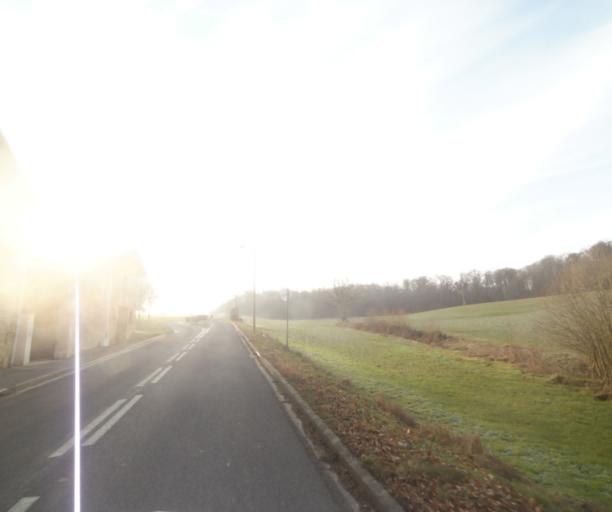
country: FR
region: Champagne-Ardenne
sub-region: Departement de la Haute-Marne
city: Chancenay
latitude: 48.7214
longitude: 4.9420
